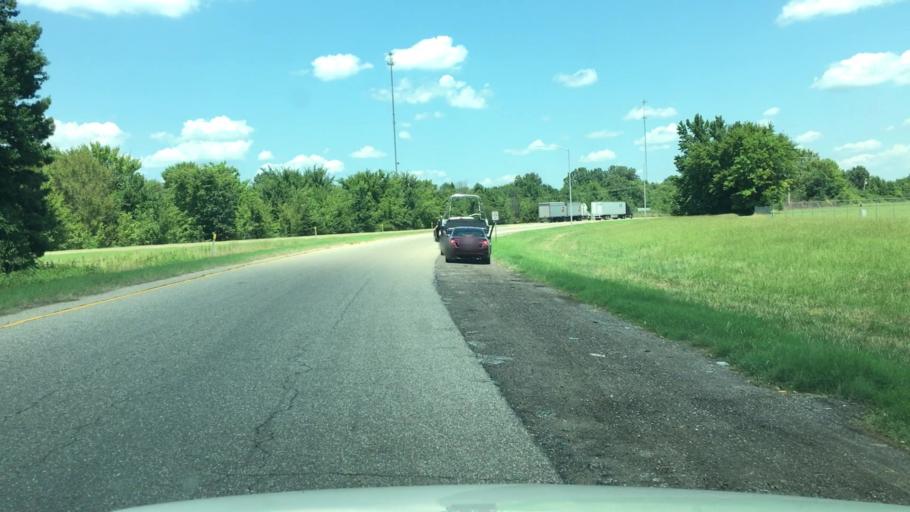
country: US
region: Arkansas
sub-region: Nevada County
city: Prescott
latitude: 33.8119
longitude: -93.4201
